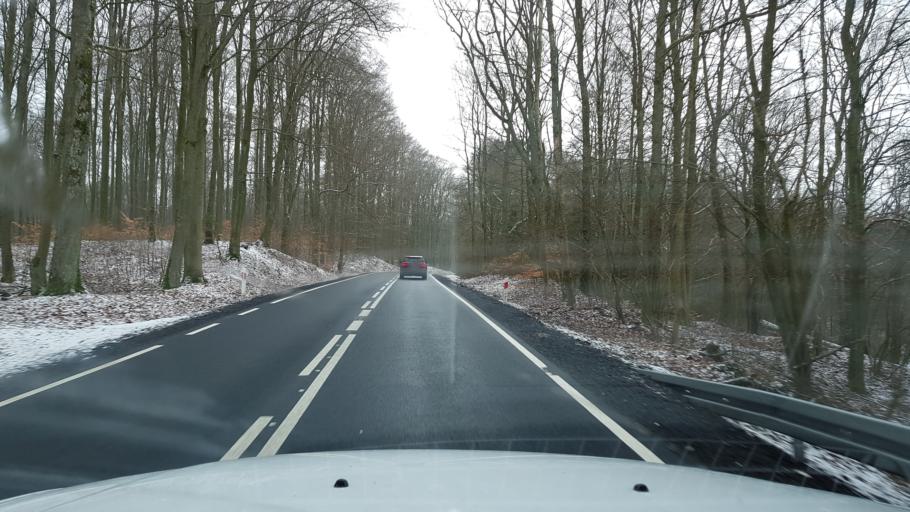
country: PL
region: West Pomeranian Voivodeship
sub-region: Powiat drawski
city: Wierzchowo
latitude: 53.5434
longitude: 16.1127
